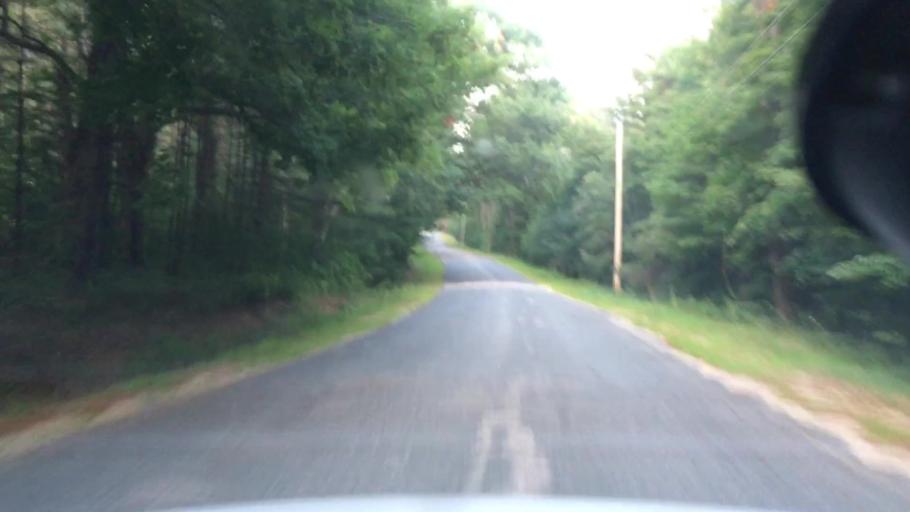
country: US
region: Maine
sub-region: Oxford County
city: Bethel
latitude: 44.4080
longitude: -70.8743
